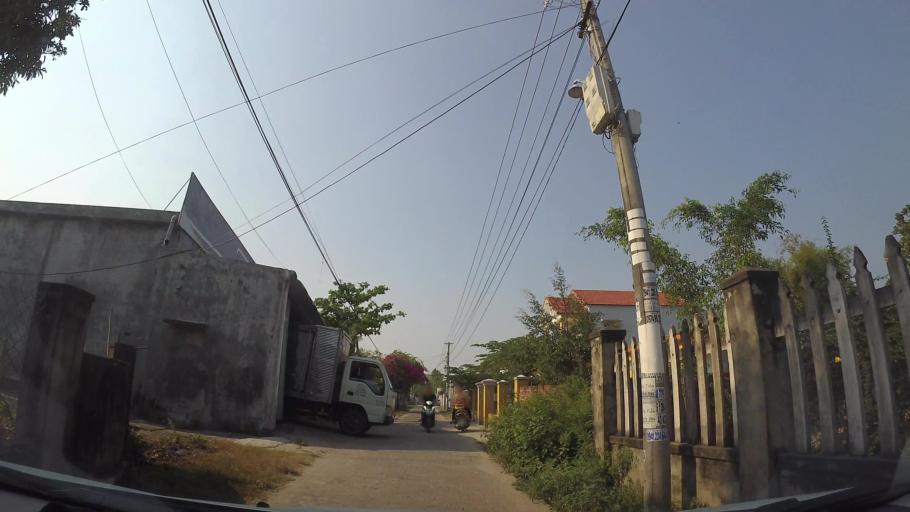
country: VN
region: Da Nang
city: Ngu Hanh Son
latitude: 15.9563
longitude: 108.2649
